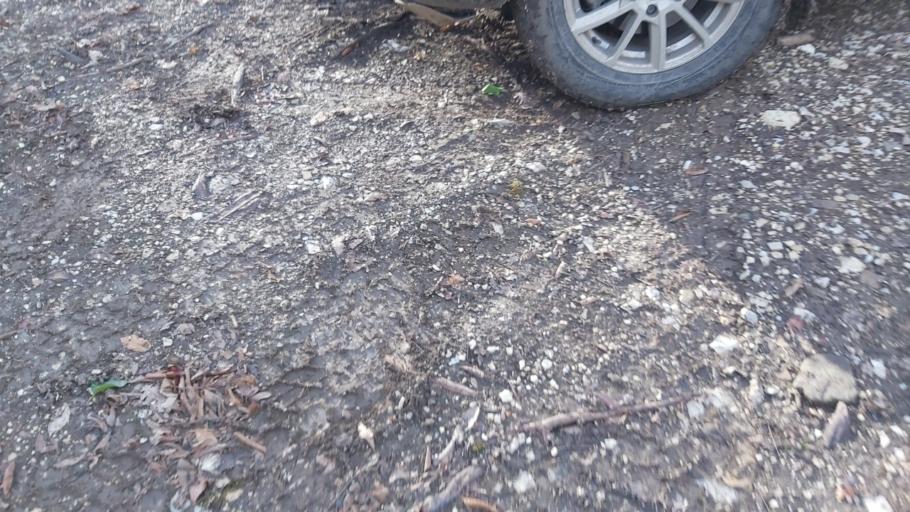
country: RU
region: Krasnodarskiy
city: Gelendzhik
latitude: 44.6088
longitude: 38.1385
